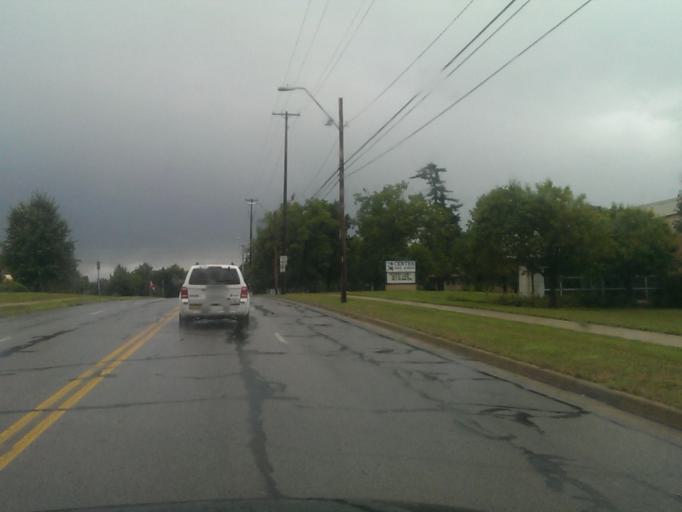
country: US
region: Kansas
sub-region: Johnson County
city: Leawood
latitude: 38.9679
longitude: -94.5814
